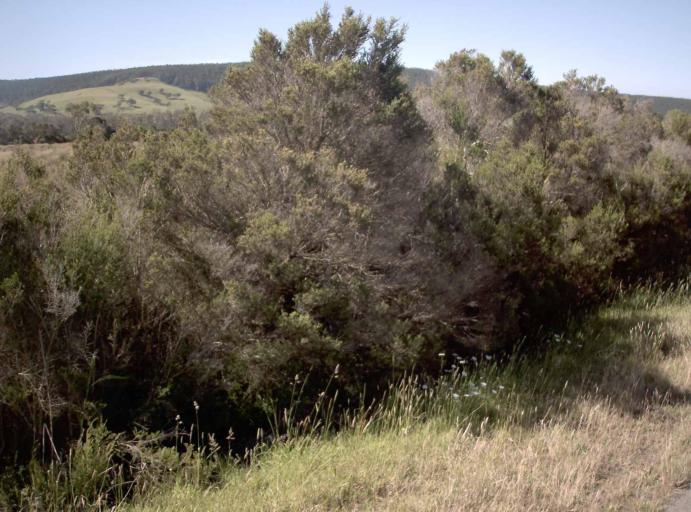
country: AU
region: Victoria
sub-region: Latrobe
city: Morwell
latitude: -38.6413
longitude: 146.5166
